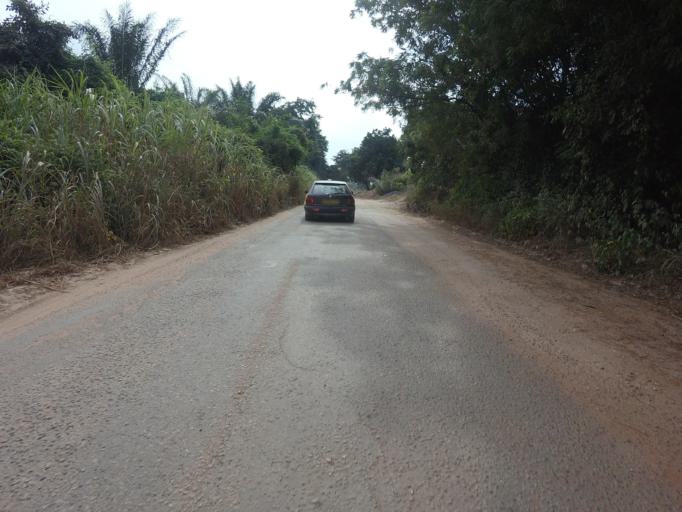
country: GH
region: Volta
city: Ho
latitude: 6.6831
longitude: 0.3370
